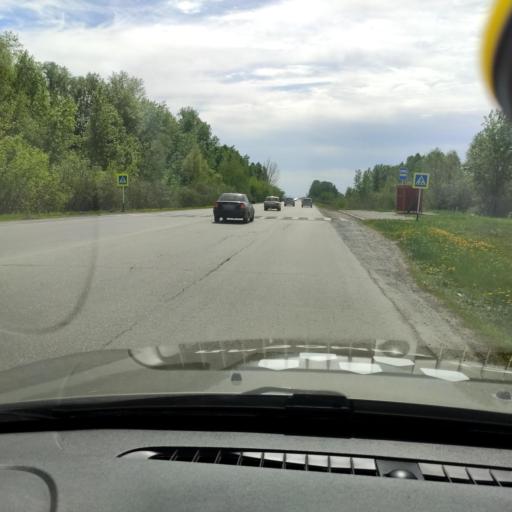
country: RU
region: Samara
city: Tol'yatti
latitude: 53.6992
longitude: 49.4203
